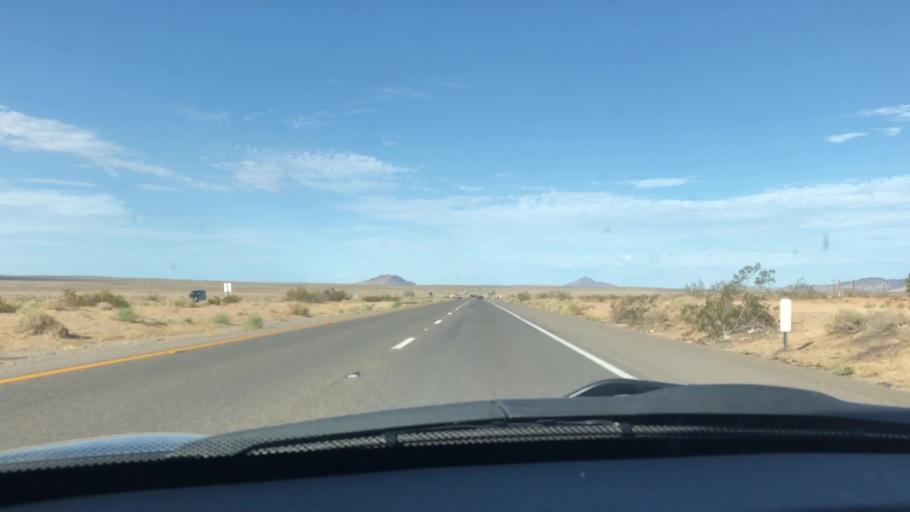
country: US
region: California
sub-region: San Bernardino County
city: Fort Irwin
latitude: 34.9883
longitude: -116.5877
